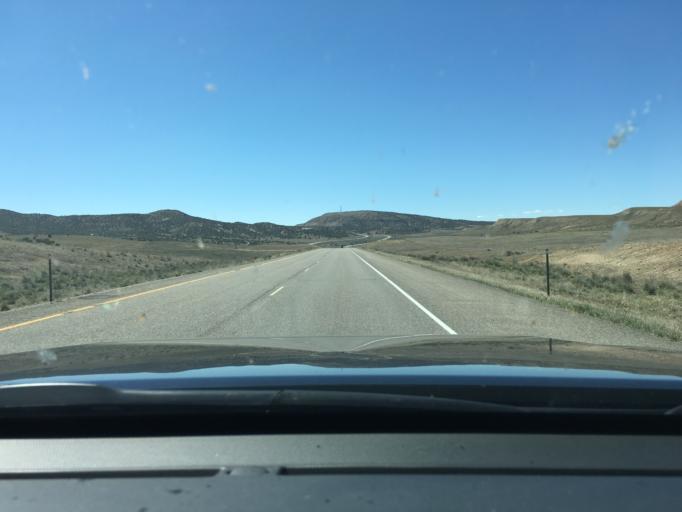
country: US
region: Colorado
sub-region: Mesa County
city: Loma
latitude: 39.2270
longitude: -108.9297
